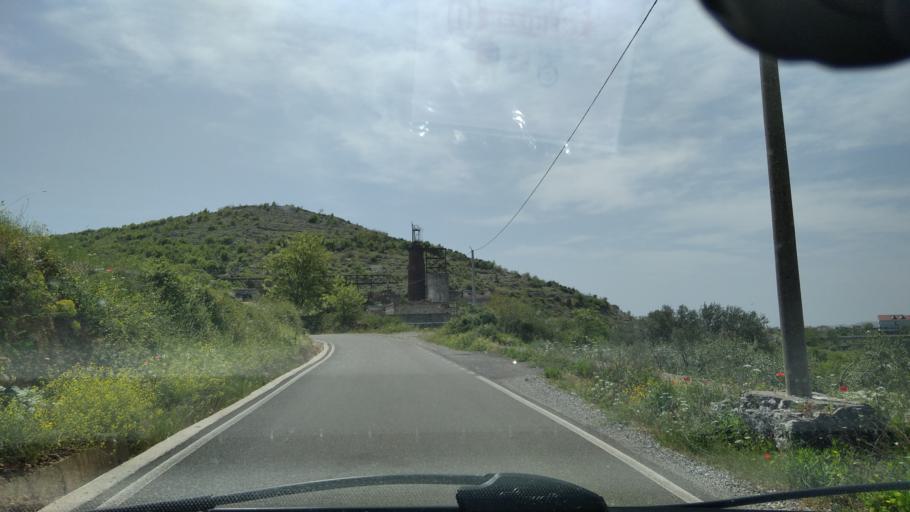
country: AL
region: Shkoder
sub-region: Rrethi i Malesia e Madhe
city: Gruemire
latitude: 42.1184
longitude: 19.5797
